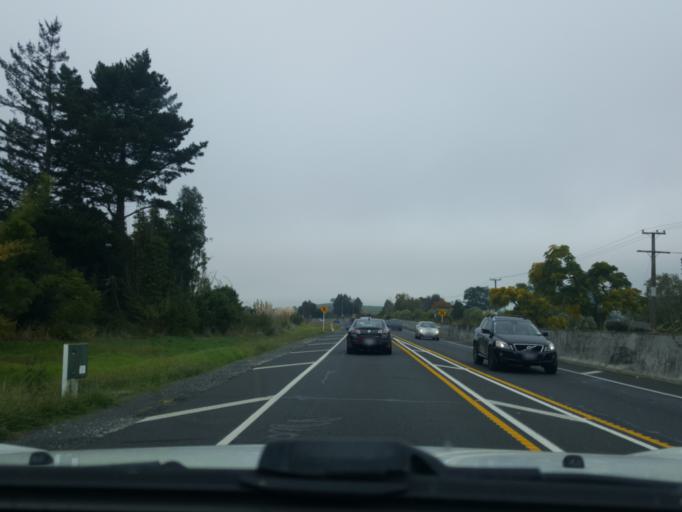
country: NZ
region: Waikato
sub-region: Waikato District
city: Ngaruawahia
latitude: -37.6135
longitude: 175.1948
